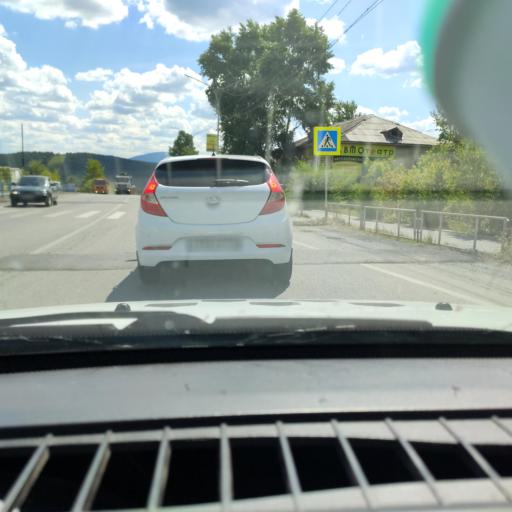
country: RU
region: Chelyabinsk
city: Satka
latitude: 55.0422
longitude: 58.9821
